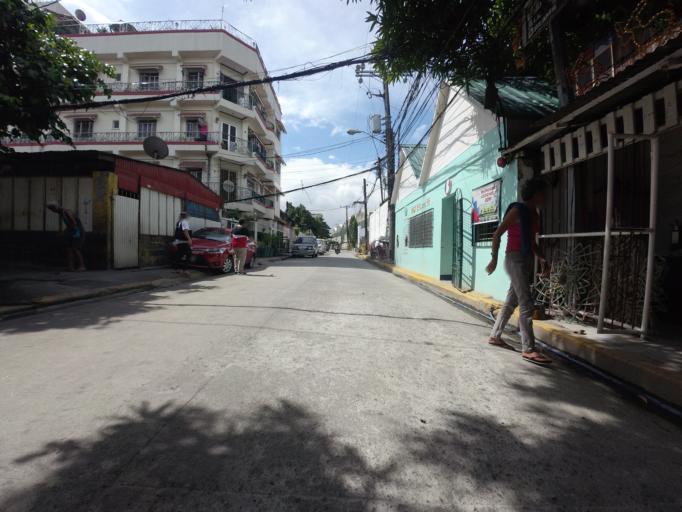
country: PH
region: Metro Manila
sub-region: San Juan
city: San Juan
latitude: 14.5849
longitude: 121.0165
